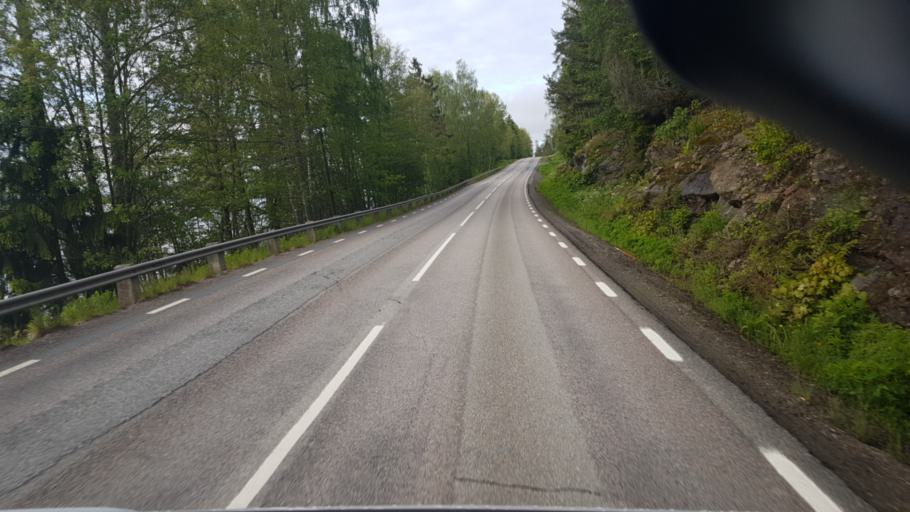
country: SE
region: Vaermland
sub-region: Eda Kommun
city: Charlottenberg
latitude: 59.8183
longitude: 12.2606
